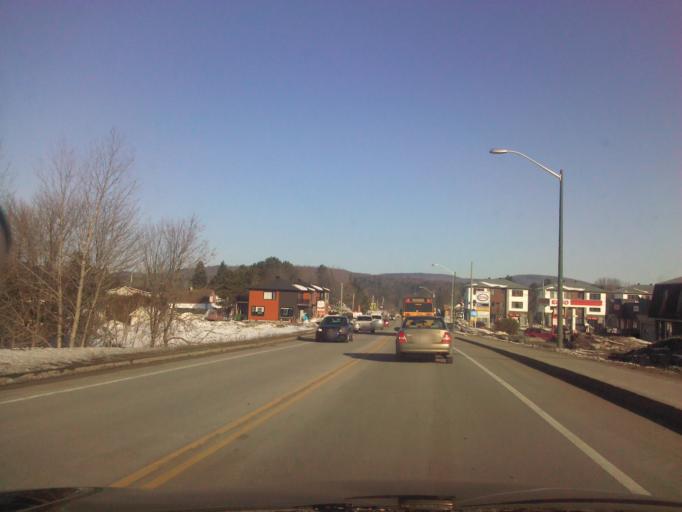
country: CA
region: Quebec
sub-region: Capitale-Nationale
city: Sainte Catherine de la Jacques Cartier
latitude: 46.8416
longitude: -71.6111
